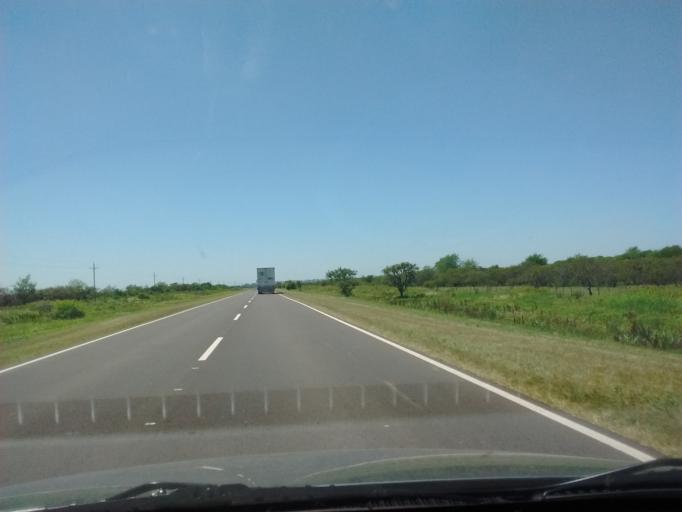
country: AR
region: Entre Rios
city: General Galarza
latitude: -32.8882
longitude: -59.6966
